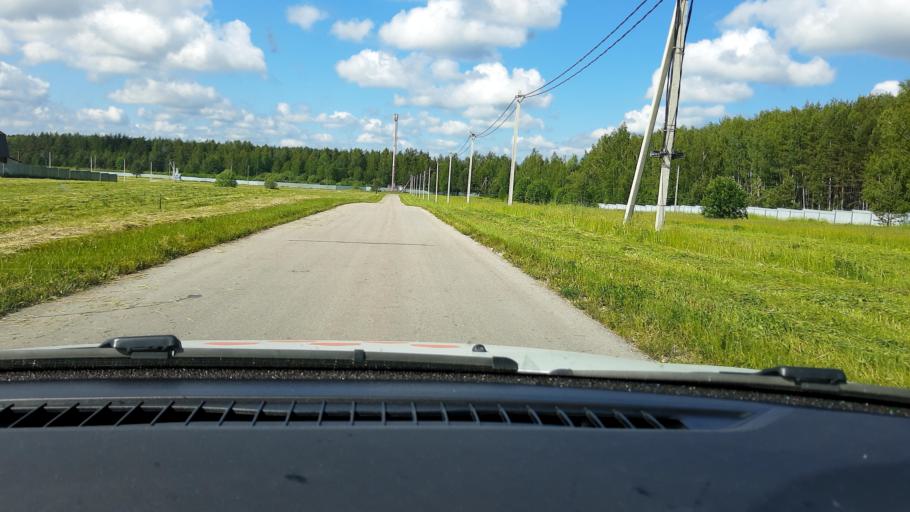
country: RU
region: Nizjnij Novgorod
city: Dal'neye Konstantinovo
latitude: 55.9277
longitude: 43.9879
